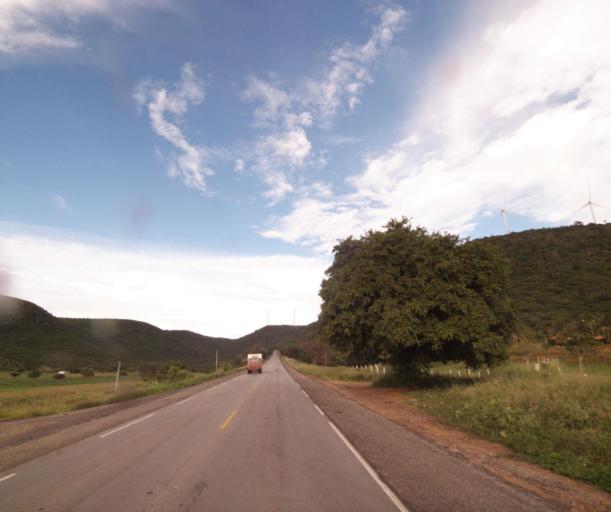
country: BR
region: Bahia
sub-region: Guanambi
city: Guanambi
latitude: -14.1567
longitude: -42.7064
